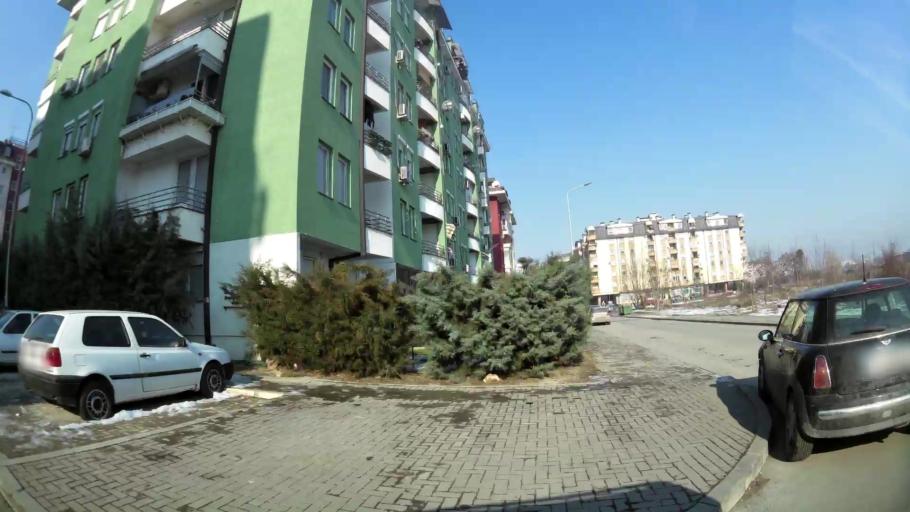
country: MK
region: Kisela Voda
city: Usje
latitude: 41.9751
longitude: 21.4460
